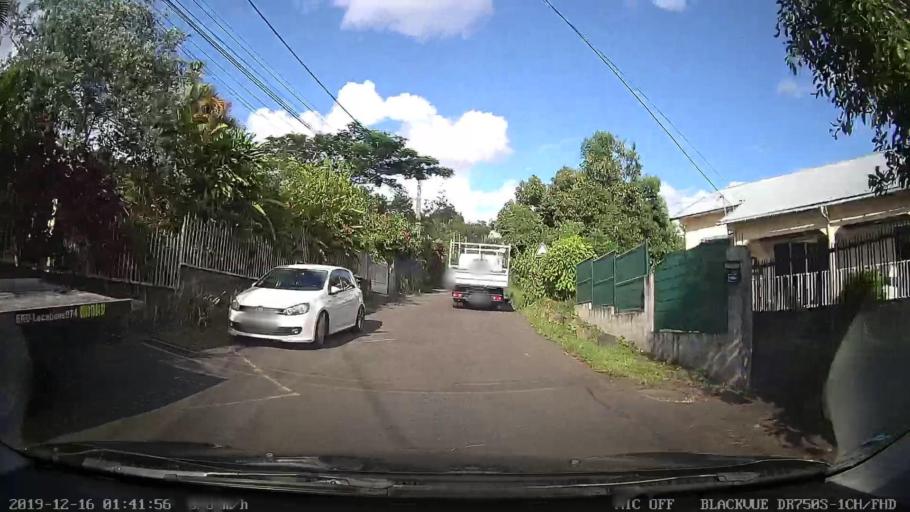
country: RE
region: Reunion
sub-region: Reunion
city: Le Tampon
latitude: -21.2546
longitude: 55.5102
